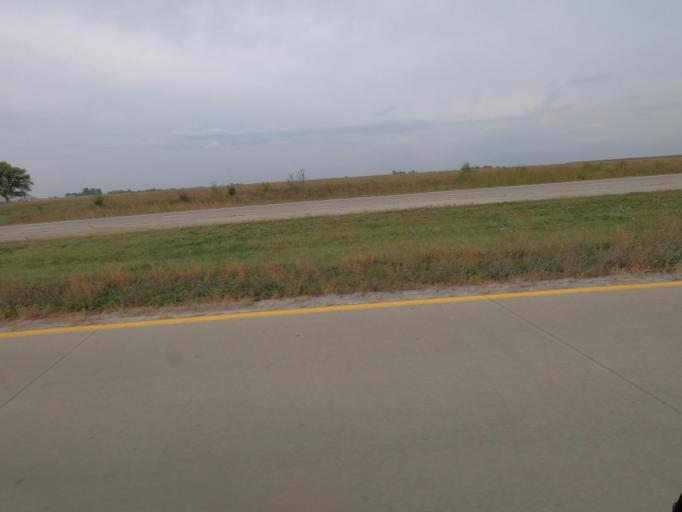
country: US
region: Iowa
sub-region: Marion County
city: Pella
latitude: 41.3700
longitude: -92.7989
